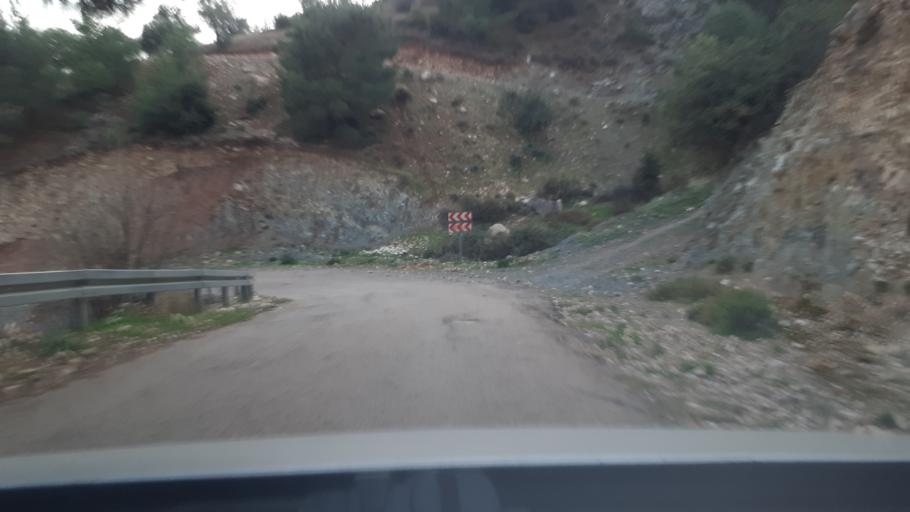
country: TR
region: Hatay
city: Kirikhan
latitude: 36.5310
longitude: 36.3157
